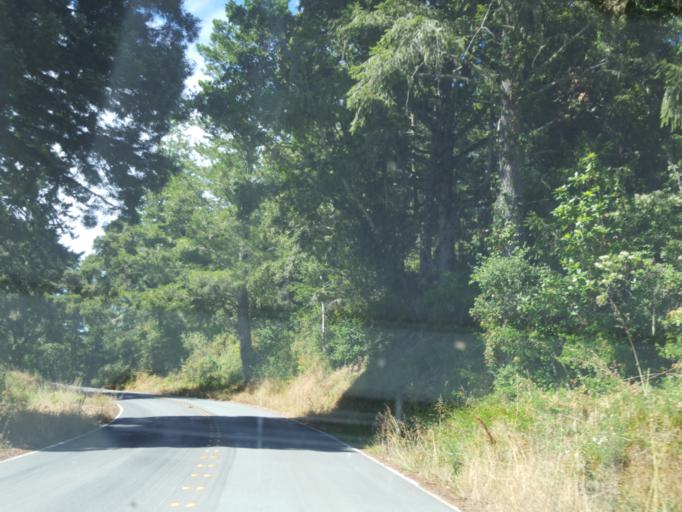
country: US
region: California
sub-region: San Mateo County
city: Portola Valley
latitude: 37.3002
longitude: -122.2763
